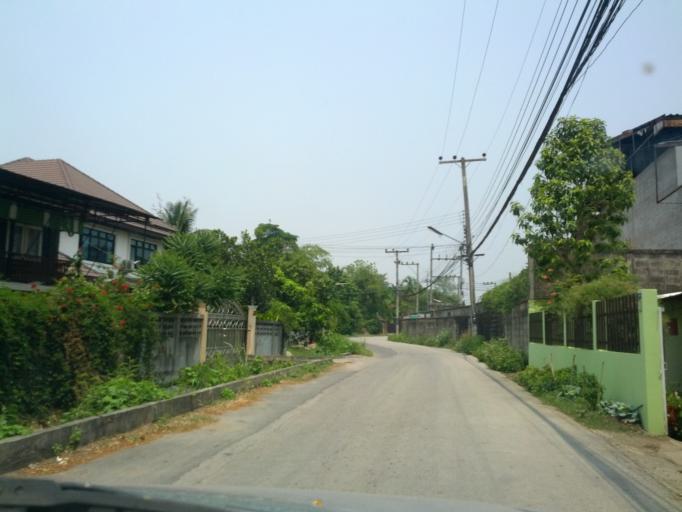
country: TH
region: Chiang Mai
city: San Sai
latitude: 18.8579
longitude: 99.1026
